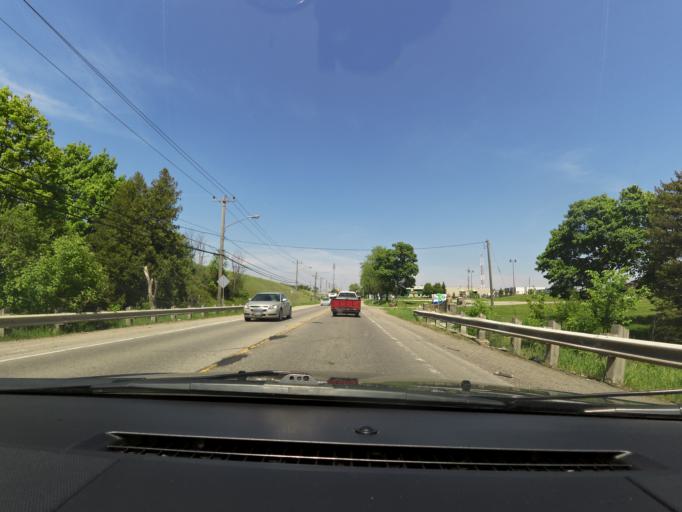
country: CA
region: Ontario
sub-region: Wellington County
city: Guelph
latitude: 43.5610
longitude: -80.2114
